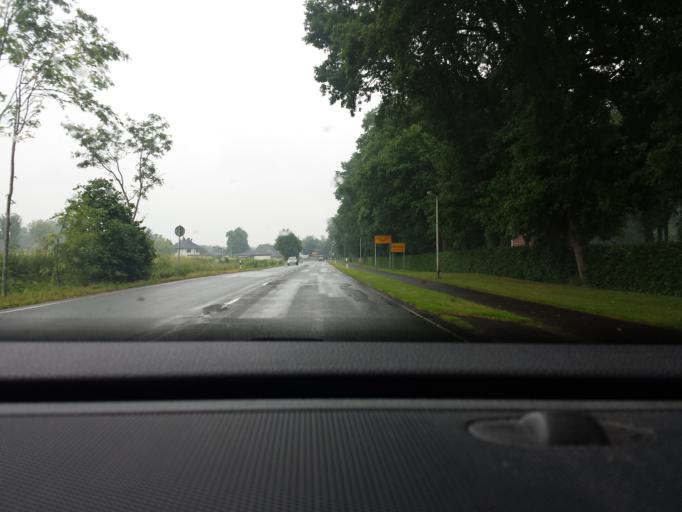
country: DE
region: North Rhine-Westphalia
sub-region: Regierungsbezirk Munster
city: Gronau
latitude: 52.2127
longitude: 6.9856
